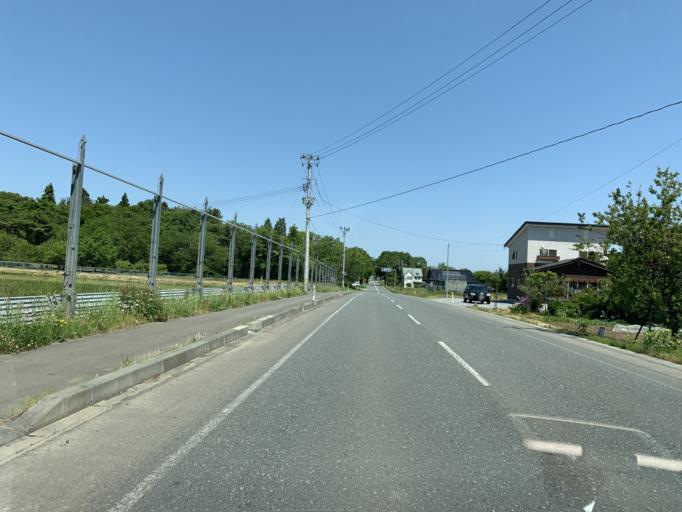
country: JP
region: Iwate
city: Kitakami
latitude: 39.2488
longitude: 141.0661
